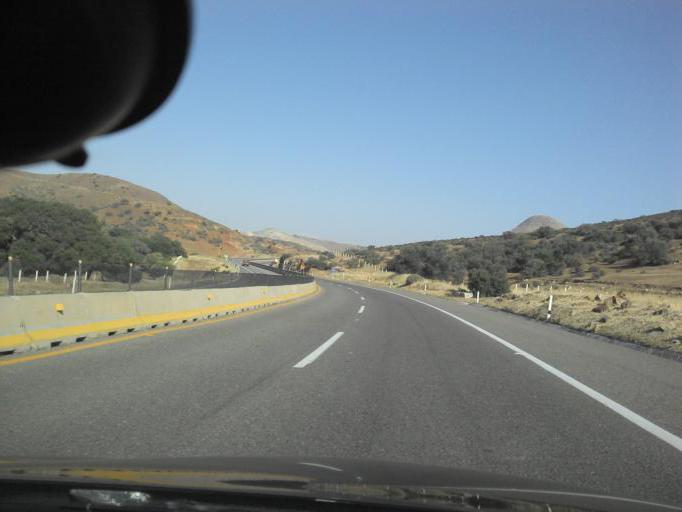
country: MX
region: Baja California
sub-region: Tijuana
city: El Nino
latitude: 32.5502
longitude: -116.8033
